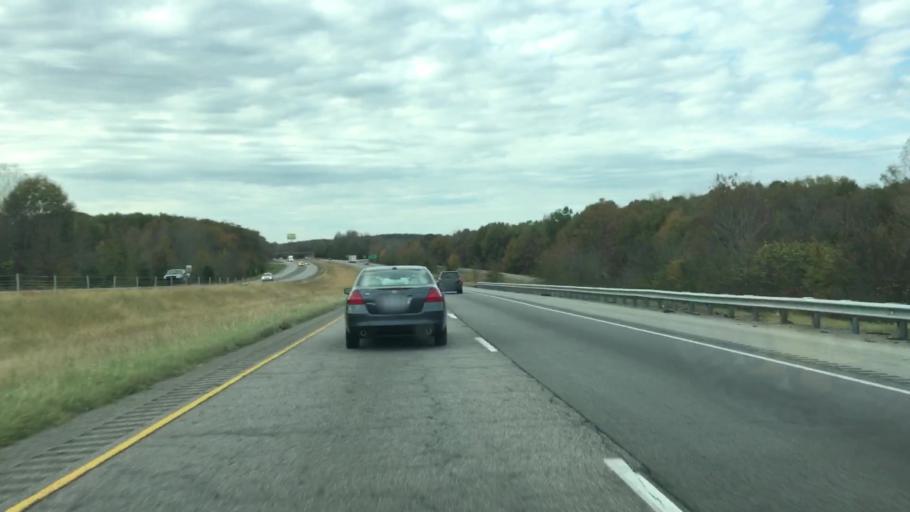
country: US
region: Arkansas
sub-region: Faulkner County
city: Conway
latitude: 35.1498
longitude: -92.5441
